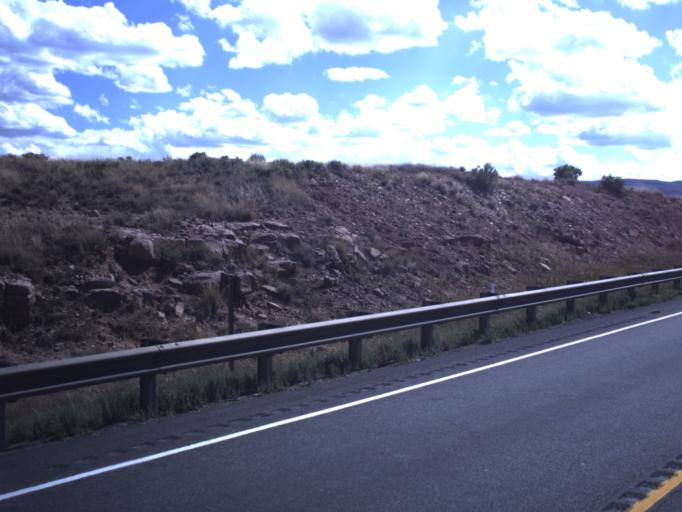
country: US
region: Utah
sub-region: Duchesne County
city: Duchesne
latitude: 40.2082
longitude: -110.7673
